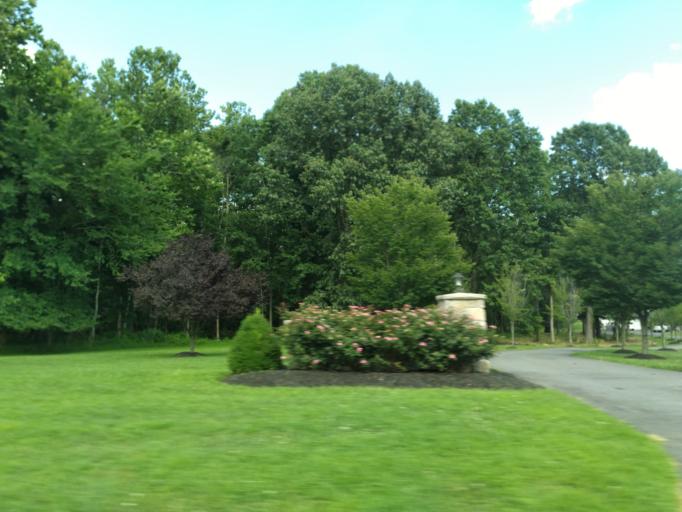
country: US
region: Maryland
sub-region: Anne Arundel County
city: Deale
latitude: 38.7960
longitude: -76.5740
